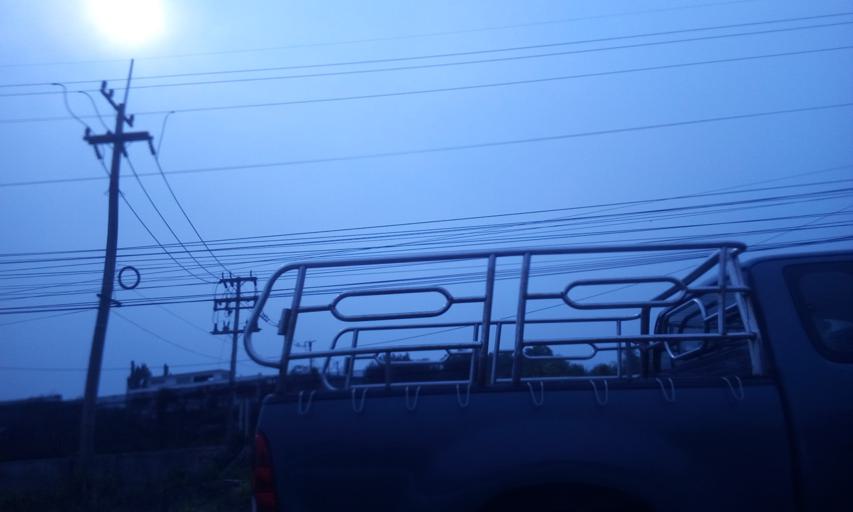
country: TH
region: Chachoengsao
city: Plaeng Yao
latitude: 13.5580
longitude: 101.2660
